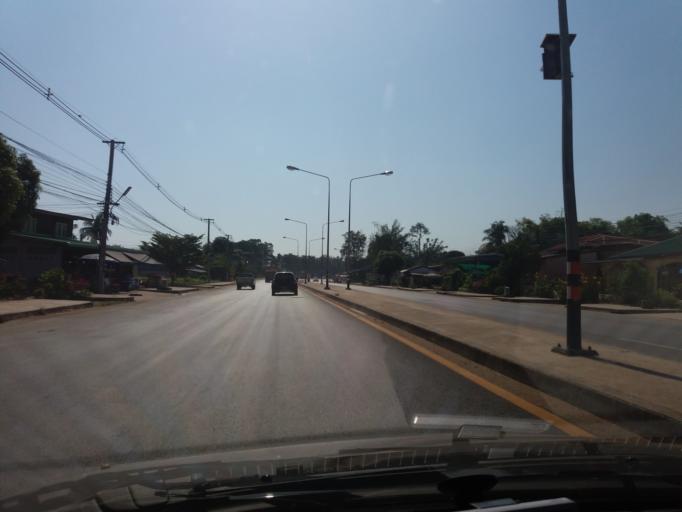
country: TH
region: Kamphaeng Phet
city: Khlong Khlung
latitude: 16.1732
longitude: 99.7965
